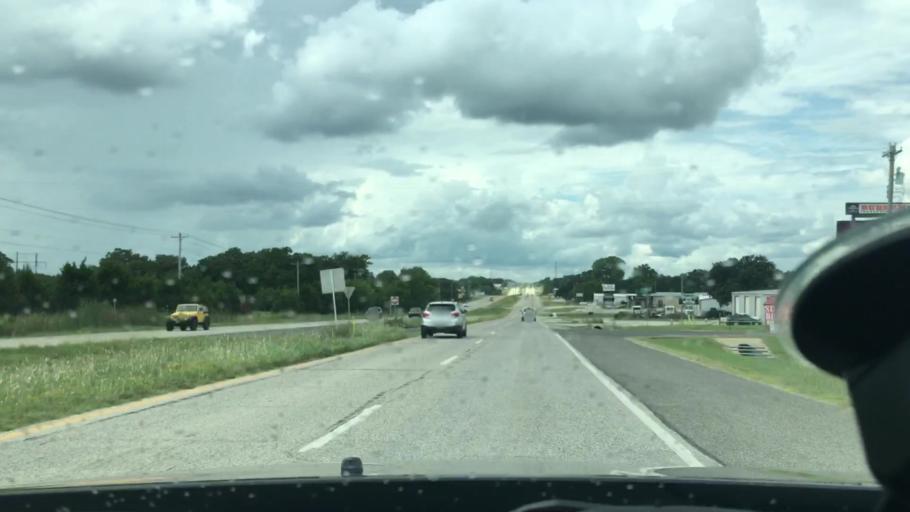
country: US
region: Oklahoma
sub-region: Carter County
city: Lone Grove
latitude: 34.1730
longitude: -97.2224
